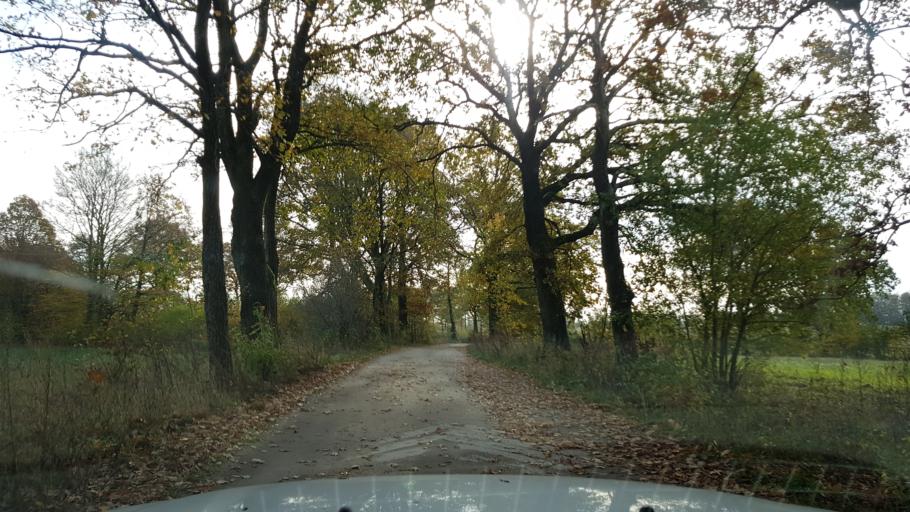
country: PL
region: West Pomeranian Voivodeship
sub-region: Powiat swidwinski
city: Polczyn-Zdroj
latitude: 53.7516
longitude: 16.0320
